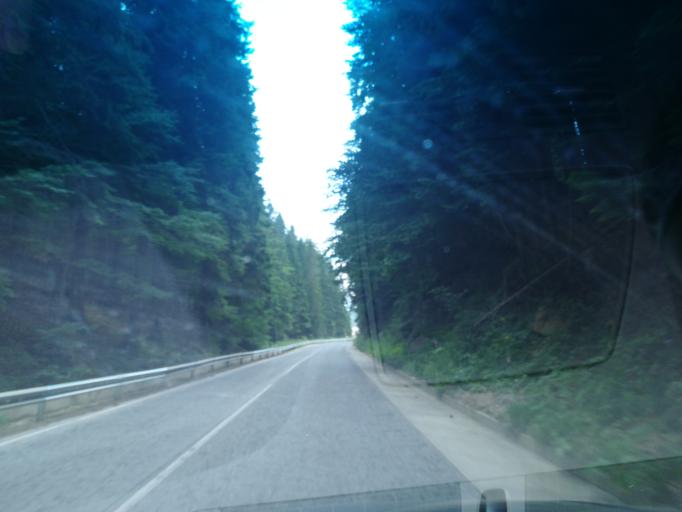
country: BG
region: Smolyan
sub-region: Obshtina Smolyan
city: Smolyan
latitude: 41.6546
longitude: 24.6970
